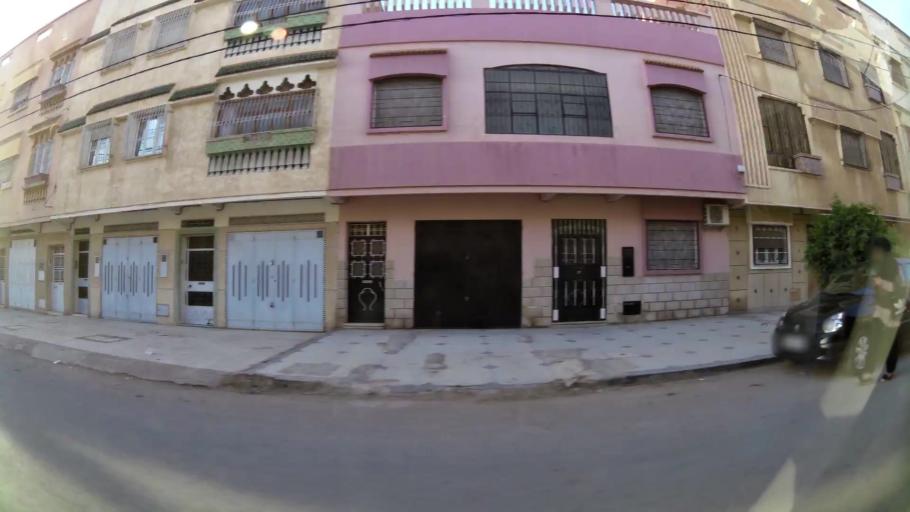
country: MA
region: Oriental
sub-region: Oujda-Angad
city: Oujda
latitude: 34.6783
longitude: -1.9017
